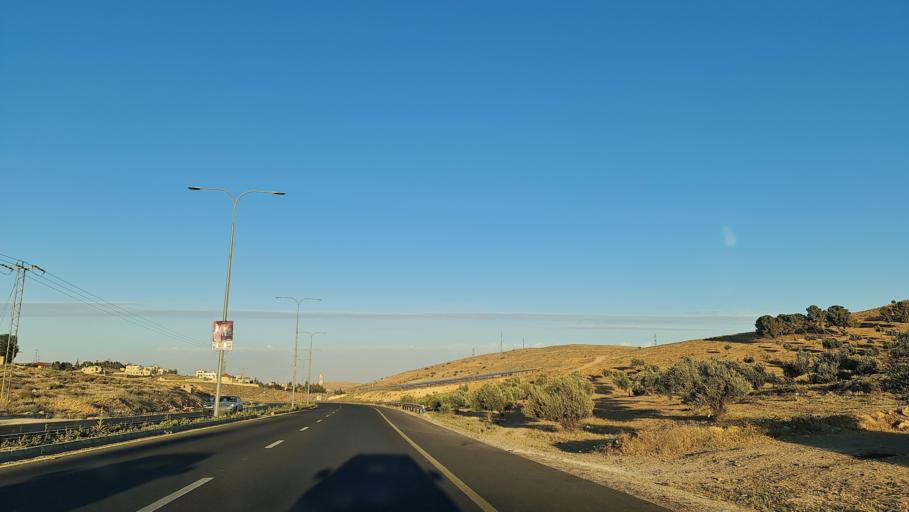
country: JO
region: Zarqa
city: Russeifa
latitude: 32.0911
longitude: 35.9798
